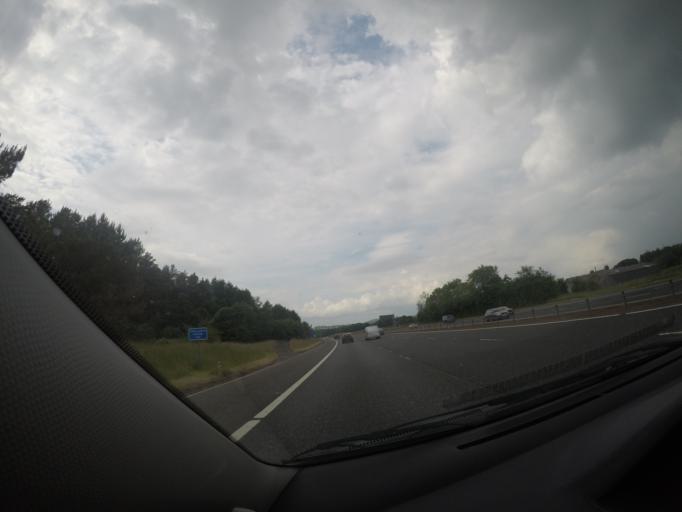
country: GB
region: Scotland
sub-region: Dumfries and Galloway
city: Lockerbie
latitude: 55.0903
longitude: -3.3203
